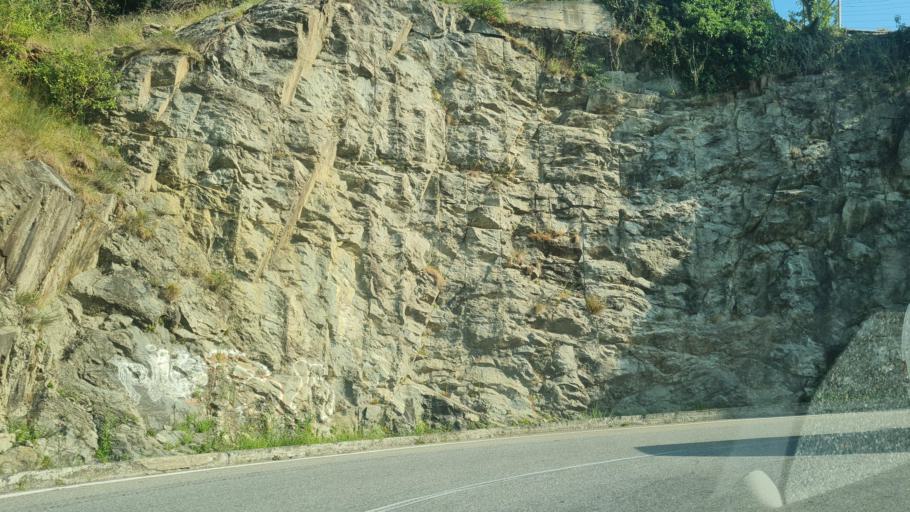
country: IT
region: Aosta Valley
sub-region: Valle d'Aosta
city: Hone
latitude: 45.6119
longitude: 7.7298
